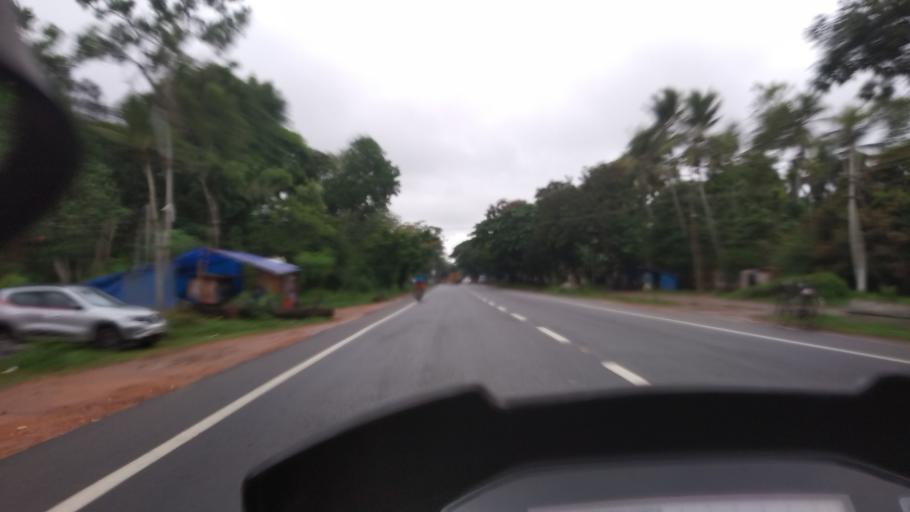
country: IN
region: Kerala
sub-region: Alappuzha
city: Mavelikara
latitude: 9.3115
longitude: 76.4301
